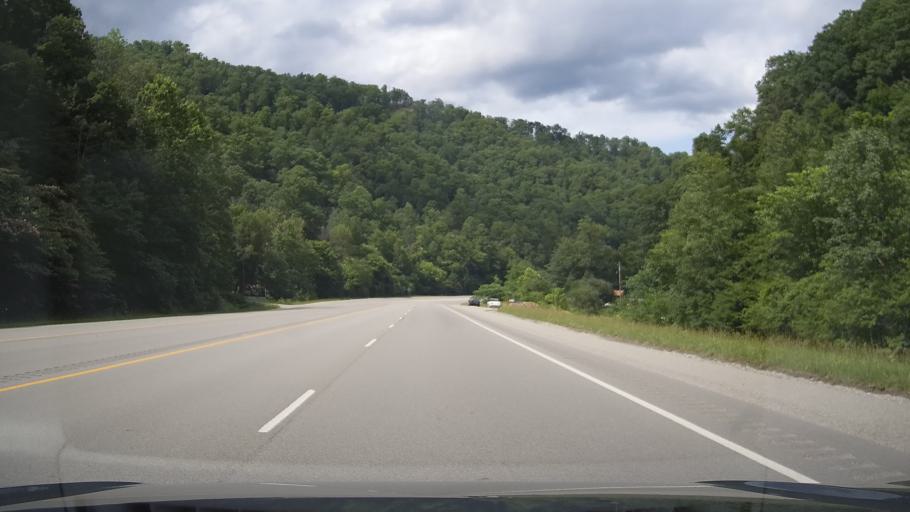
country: US
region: Kentucky
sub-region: Pike County
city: Pikeville
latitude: 37.3373
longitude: -82.5568
